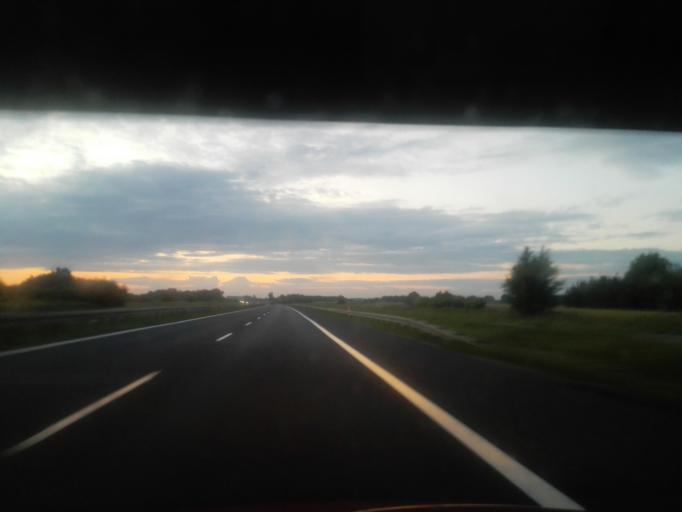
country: PL
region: Lodz Voivodeship
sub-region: Piotrkow Trybunalski
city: Piotrkow Trybunalski
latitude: 51.4427
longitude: 19.6426
